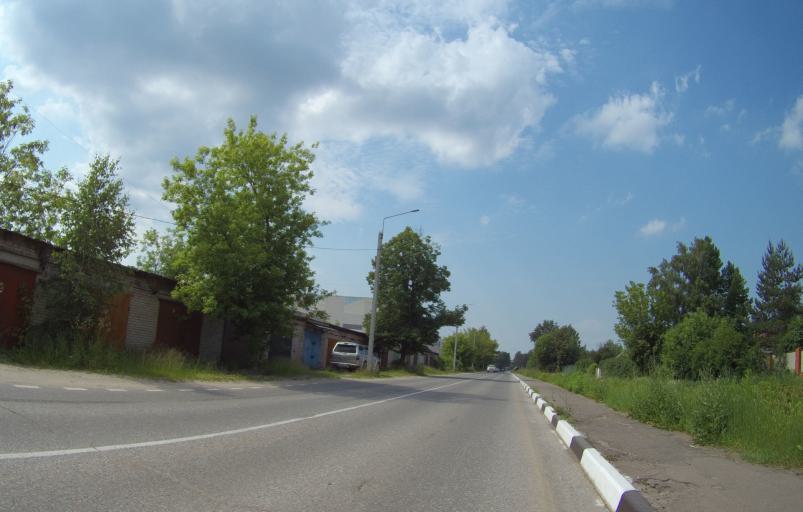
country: RU
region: Moskovskaya
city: Bykovo
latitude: 55.6166
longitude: 38.0788
